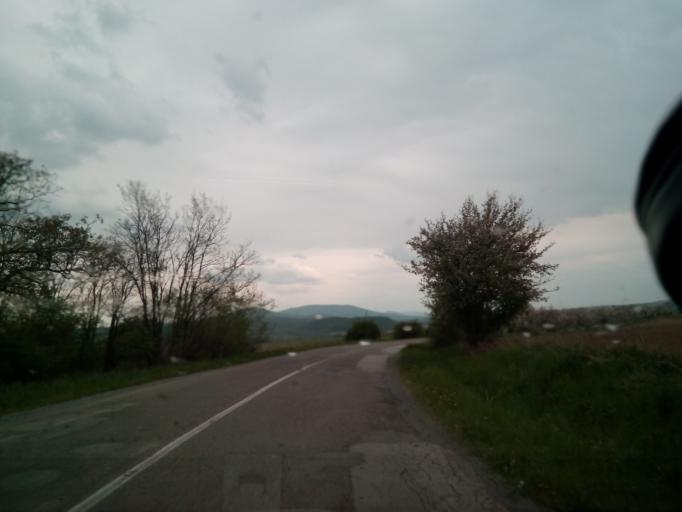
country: SK
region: Kosicky
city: Secovce
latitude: 48.7537
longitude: 21.4650
